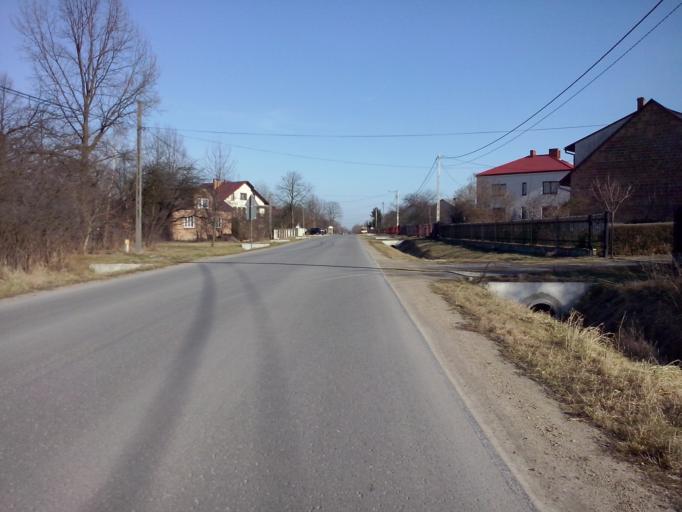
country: PL
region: Subcarpathian Voivodeship
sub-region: Powiat nizanski
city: Krzeszow
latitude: 50.4157
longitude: 22.3567
